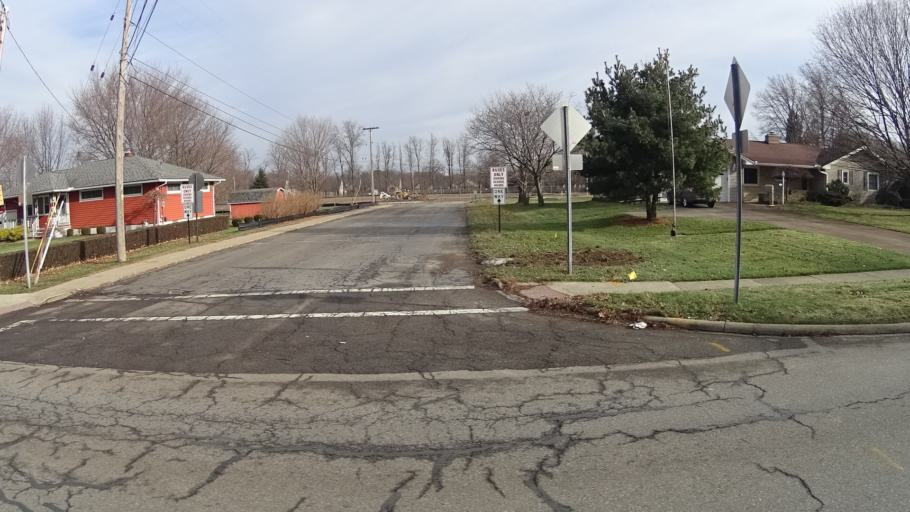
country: US
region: Ohio
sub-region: Lorain County
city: Amherst
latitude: 41.3936
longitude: -82.2395
